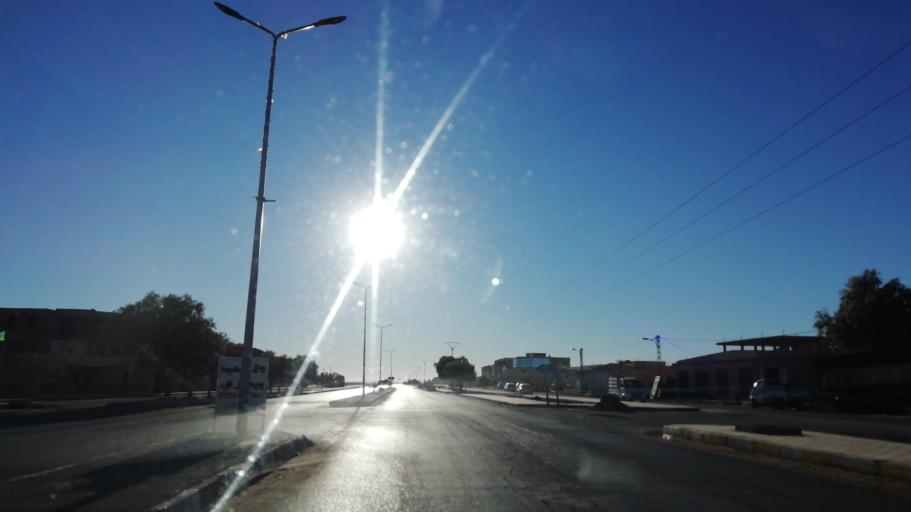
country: DZ
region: Saida
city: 'Ain el Hadjar
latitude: 34.0276
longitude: 0.0948
